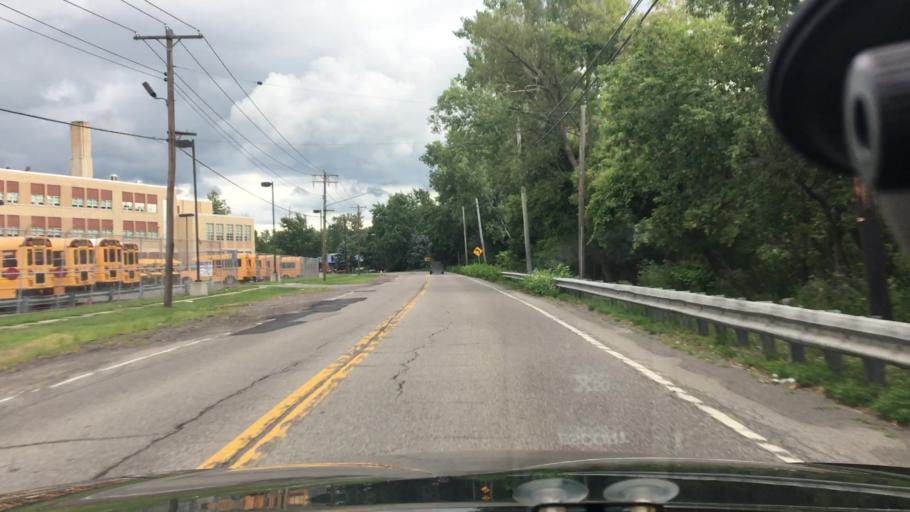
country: US
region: New York
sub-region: Erie County
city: West Seneca
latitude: 42.8338
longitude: -78.7750
